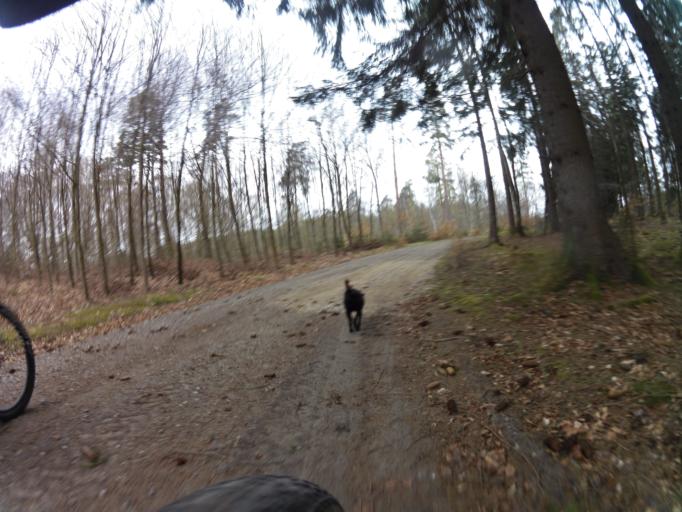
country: PL
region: West Pomeranian Voivodeship
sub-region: Powiat koszalinski
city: Polanow
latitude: 54.0662
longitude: 16.6249
